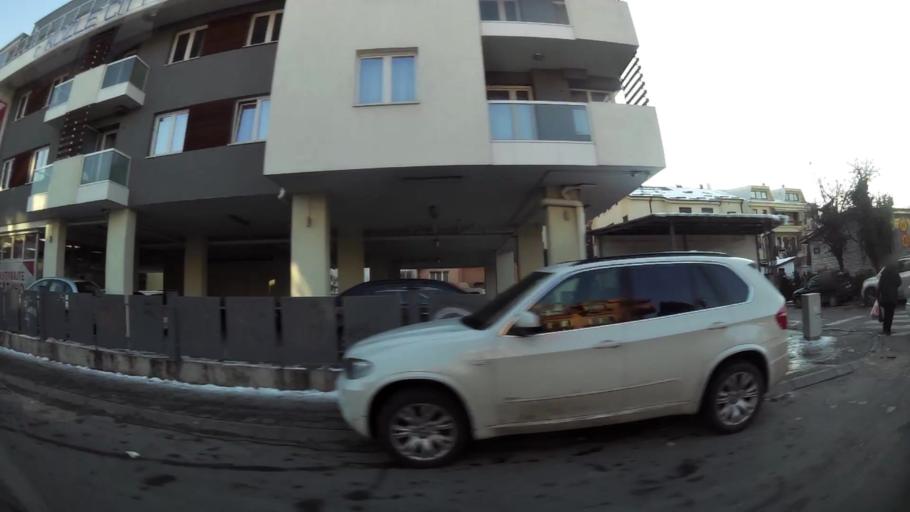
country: MK
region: Karpos
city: Skopje
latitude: 41.9940
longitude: 21.4010
